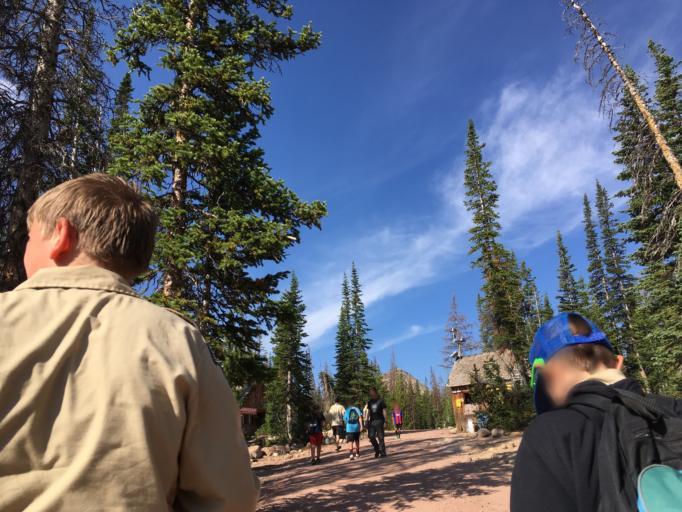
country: US
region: Utah
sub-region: Summit County
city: Kamas
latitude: 40.7198
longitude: -110.8841
